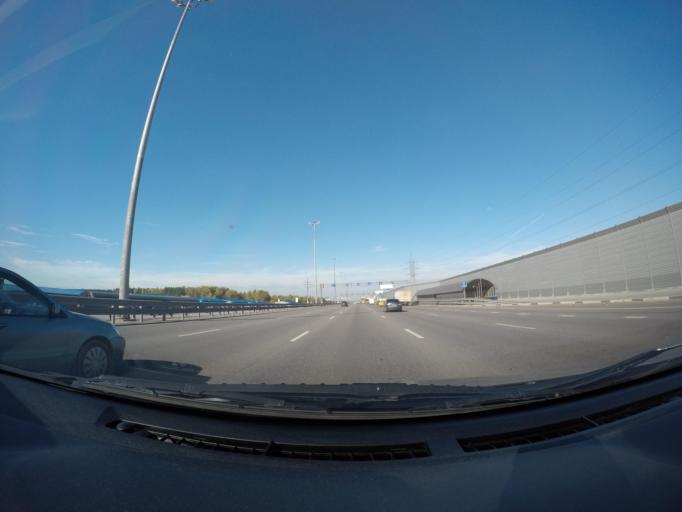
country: RU
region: Moskovskaya
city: Tomilino
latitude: 55.6370
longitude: 37.9263
